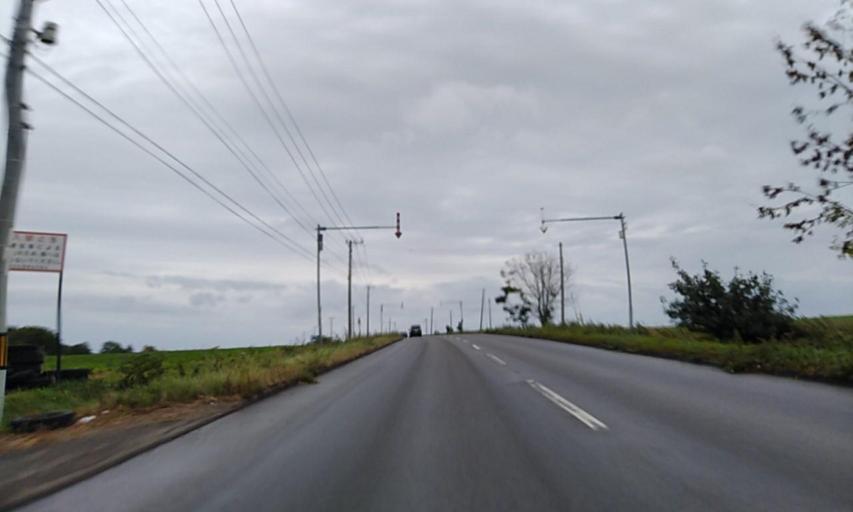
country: JP
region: Hokkaido
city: Kitami
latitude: 44.0955
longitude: 143.9598
